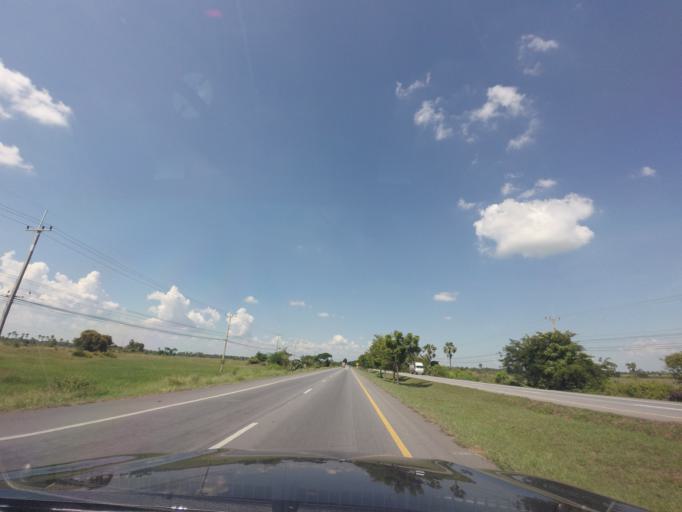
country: TH
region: Nakhon Ratchasima
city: Non Sung
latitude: 15.1326
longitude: 102.3084
